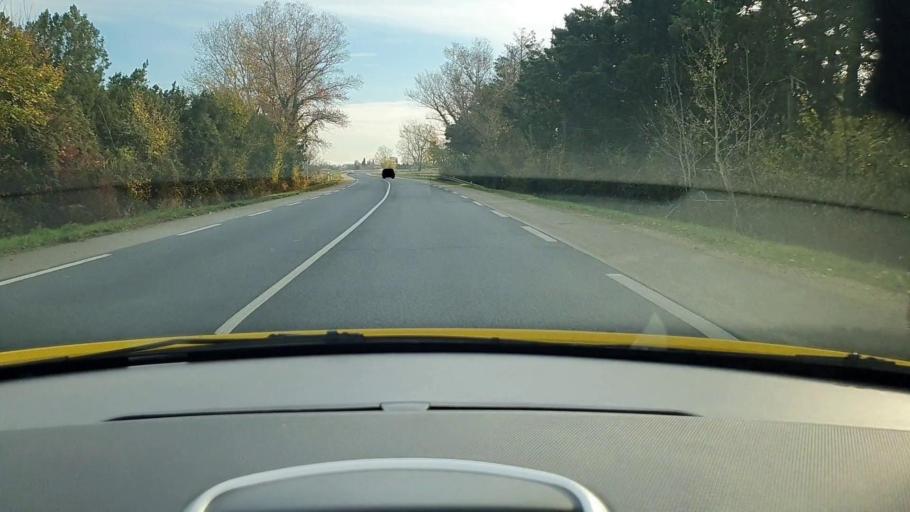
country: FR
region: Languedoc-Roussillon
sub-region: Departement du Gard
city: Fourques
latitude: 43.6995
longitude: 4.5786
